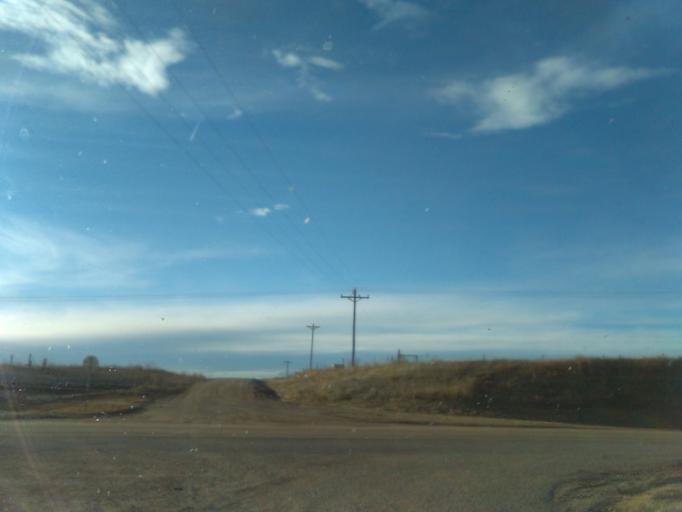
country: US
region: Nebraska
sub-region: Morrill County
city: Bridgeport
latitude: 41.4820
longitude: -102.9832
